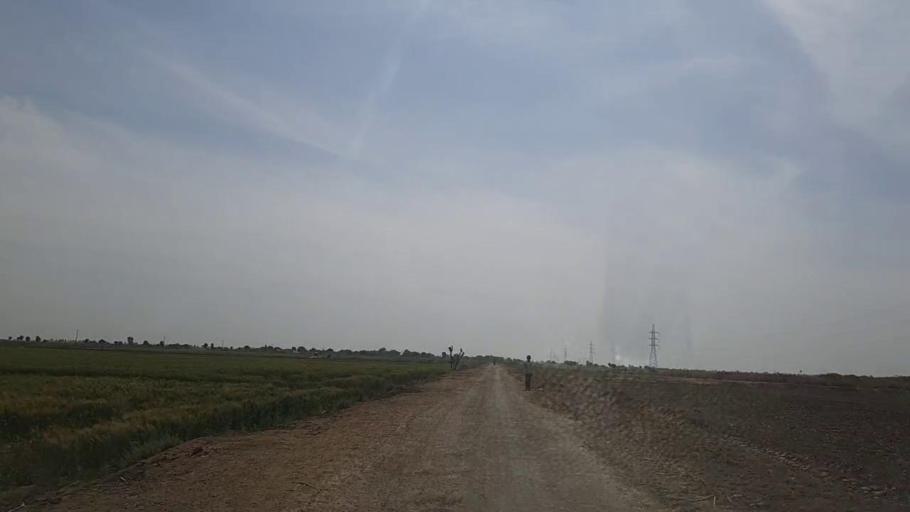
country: PK
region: Sindh
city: Kunri
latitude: 25.1763
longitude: 69.4569
